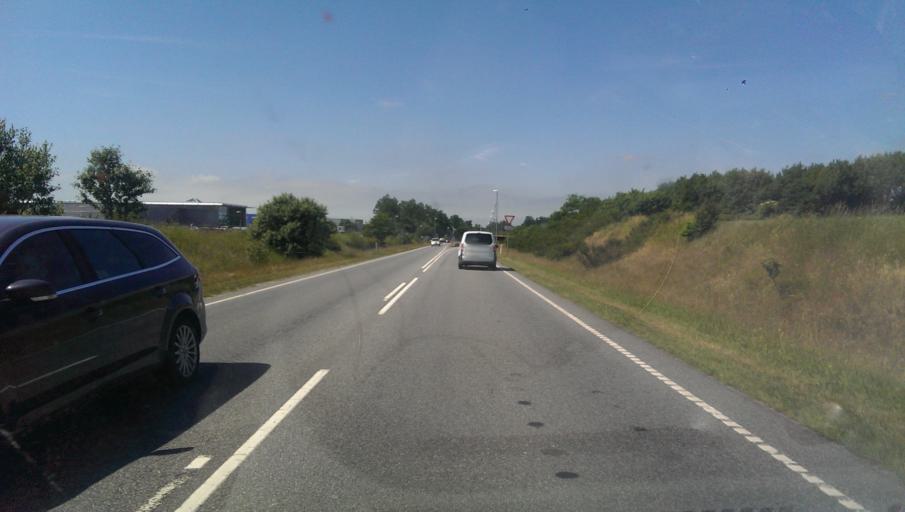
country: DK
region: South Denmark
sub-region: Esbjerg Kommune
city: Esbjerg
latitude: 55.5172
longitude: 8.4723
